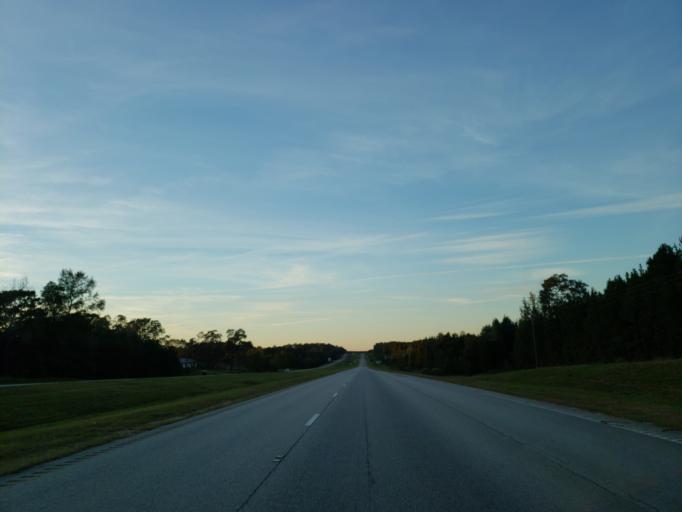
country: US
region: Mississippi
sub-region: Wayne County
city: Belmont
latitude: 31.4642
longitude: -88.4716
